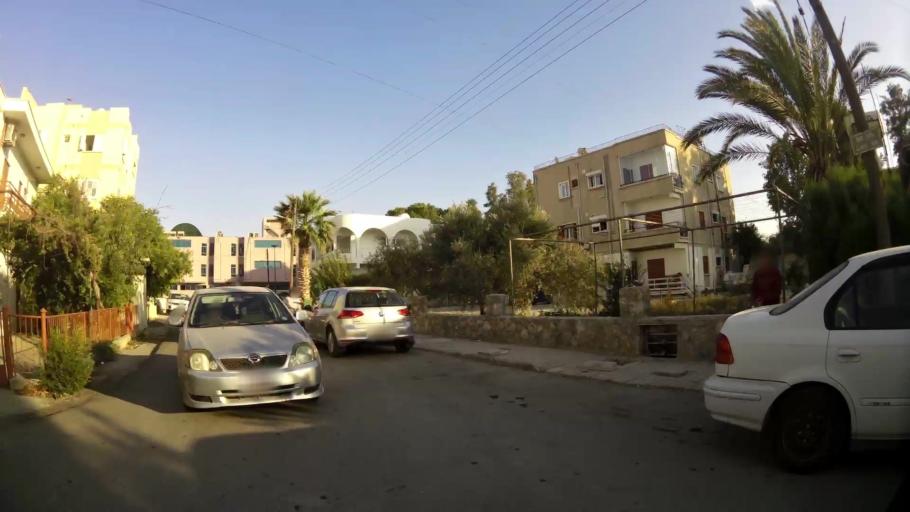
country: CY
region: Lefkosia
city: Nicosia
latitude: 35.1873
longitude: 33.3541
